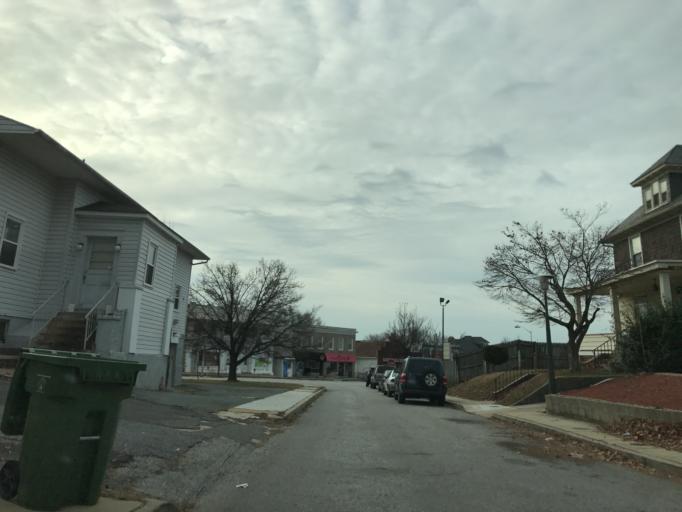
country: US
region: Maryland
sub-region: Baltimore County
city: Overlea
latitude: 39.3524
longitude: -76.5343
